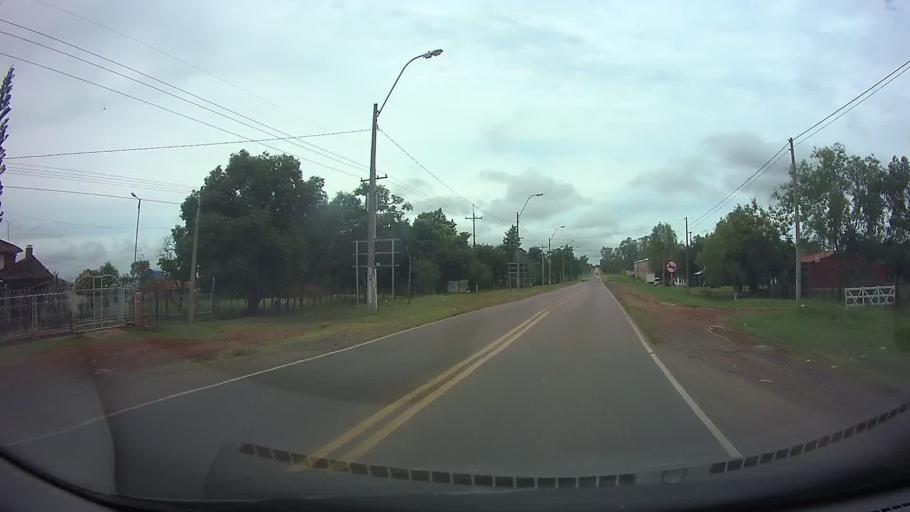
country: PY
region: Paraguari
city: Carapegua
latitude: -25.7715
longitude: -57.2328
